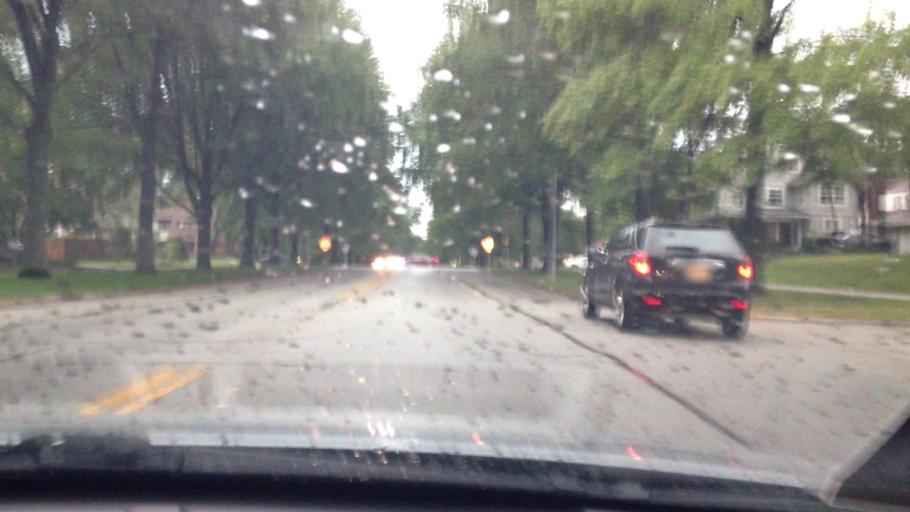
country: US
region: Kansas
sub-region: Johnson County
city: Mission Hills
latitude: 39.0121
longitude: -94.5871
